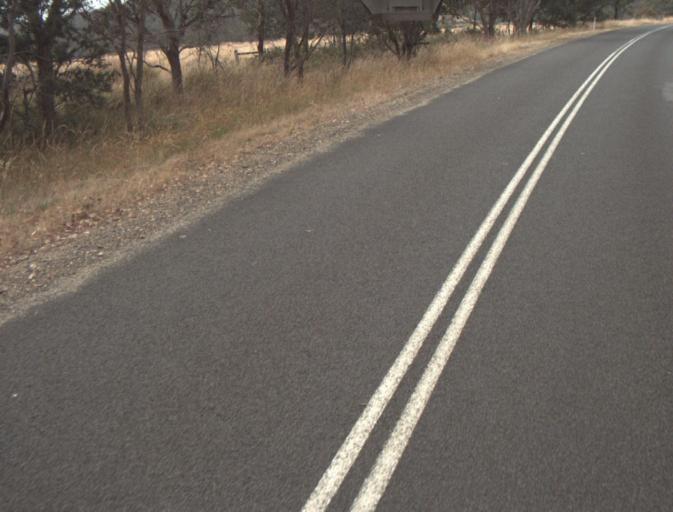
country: AU
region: Tasmania
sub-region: Northern Midlands
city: Evandale
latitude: -41.5071
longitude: 147.3605
